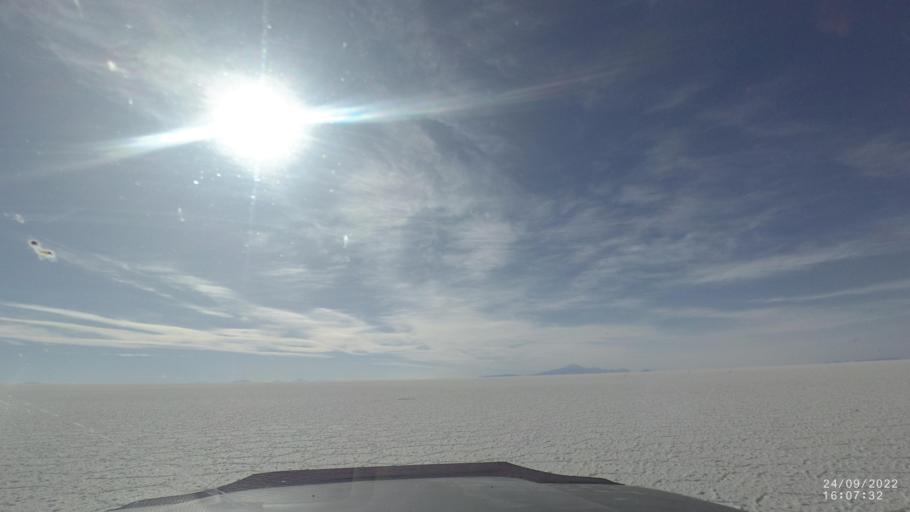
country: BO
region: Potosi
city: Colchani
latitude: -20.2988
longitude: -67.3033
